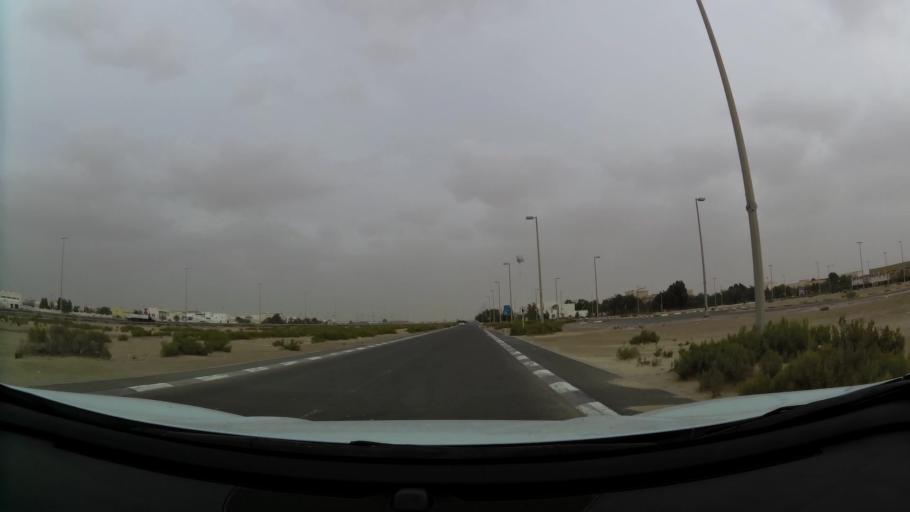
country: AE
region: Abu Dhabi
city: Abu Dhabi
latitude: 24.3723
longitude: 54.6648
